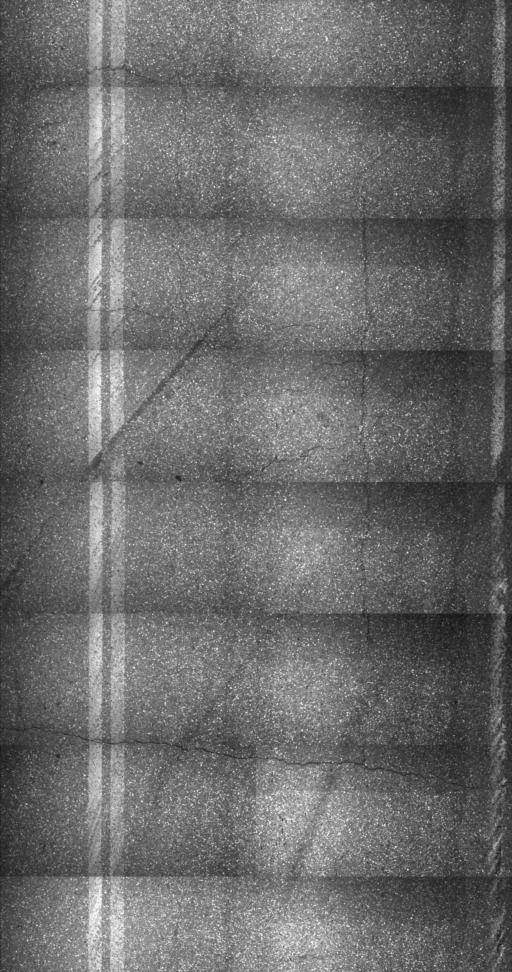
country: US
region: Vermont
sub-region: Lamoille County
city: Morristown
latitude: 44.5509
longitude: -72.6155
